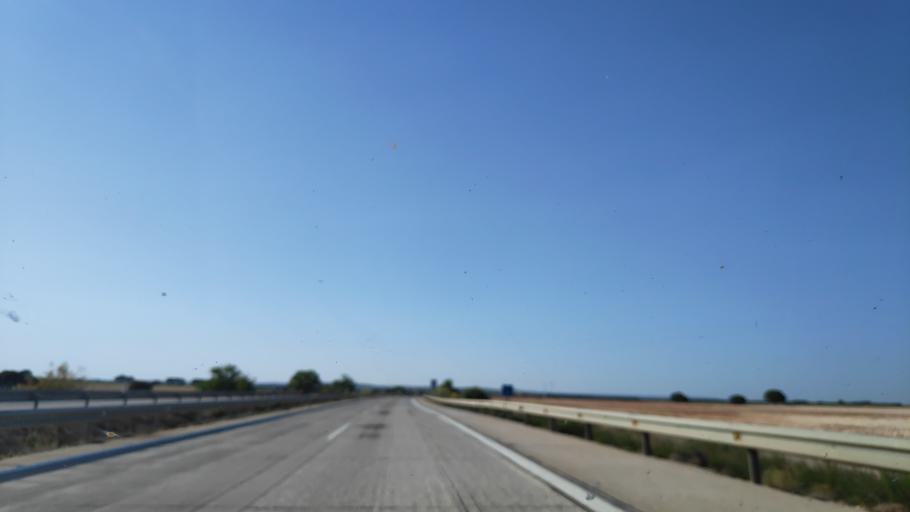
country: ES
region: Castille-La Mancha
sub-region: Provincia de Cuenca
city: Casas de Guijarro
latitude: 39.3076
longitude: -2.2024
